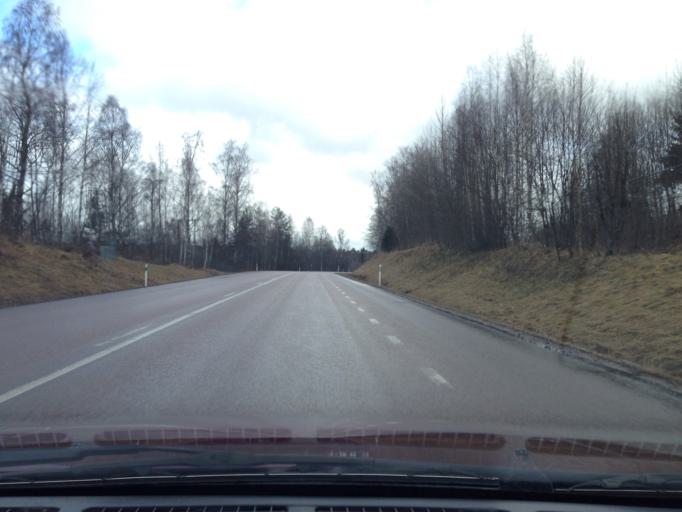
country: SE
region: Dalarna
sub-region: Ludvika Kommun
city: Ludvika
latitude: 60.1524
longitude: 15.2269
